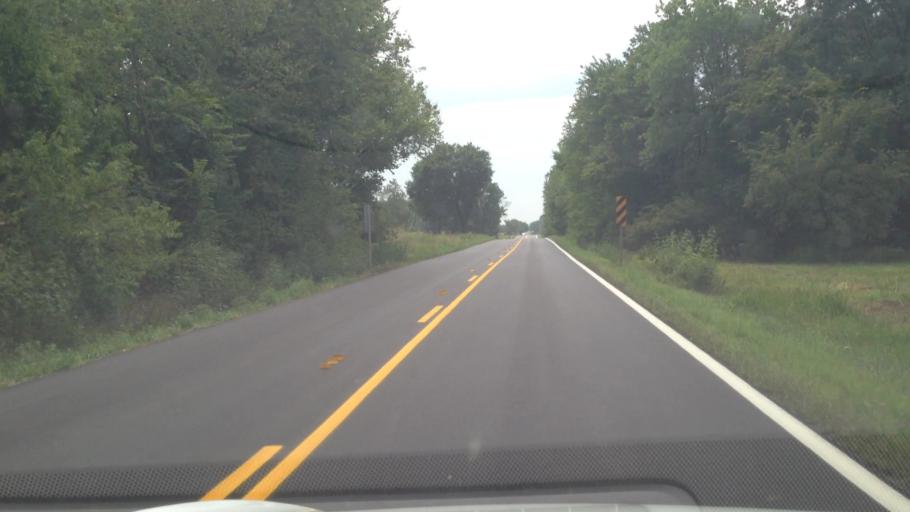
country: US
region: Kansas
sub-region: Crawford County
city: Girard
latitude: 37.5224
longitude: -94.9606
